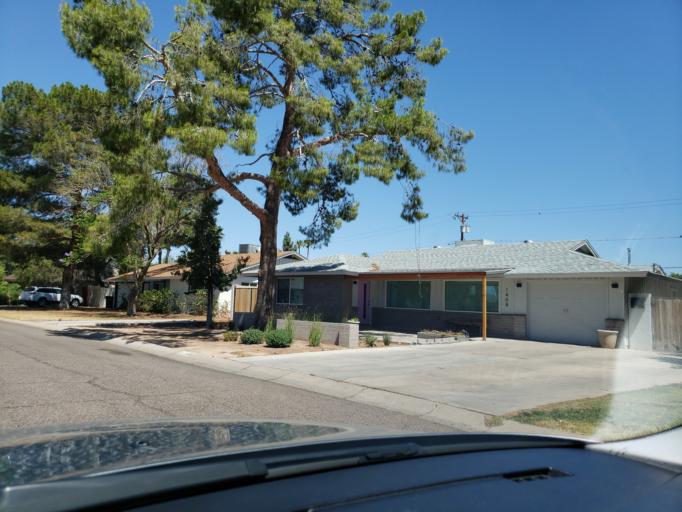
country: US
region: Arizona
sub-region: Maricopa County
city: Phoenix
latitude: 33.5108
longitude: -112.0903
